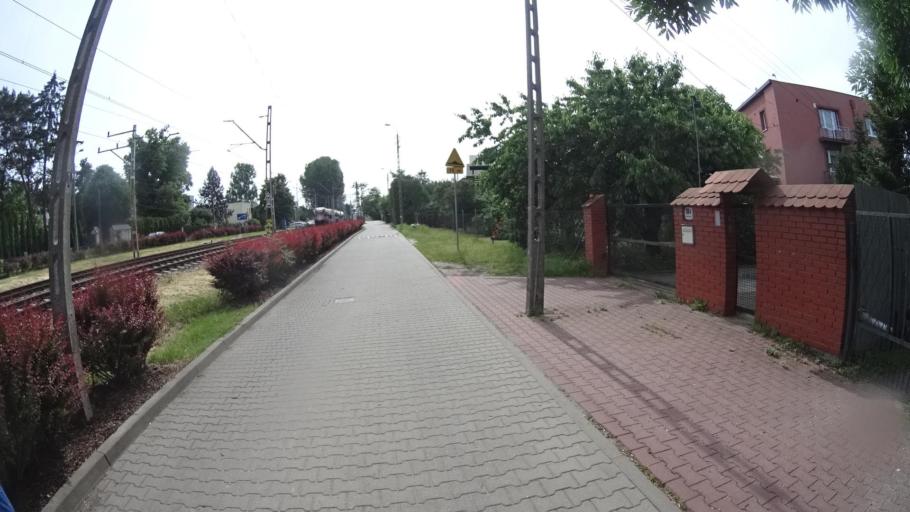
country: PL
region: Masovian Voivodeship
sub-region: Powiat pruszkowski
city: Nowe Grocholice
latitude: 52.1821
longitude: 20.9069
